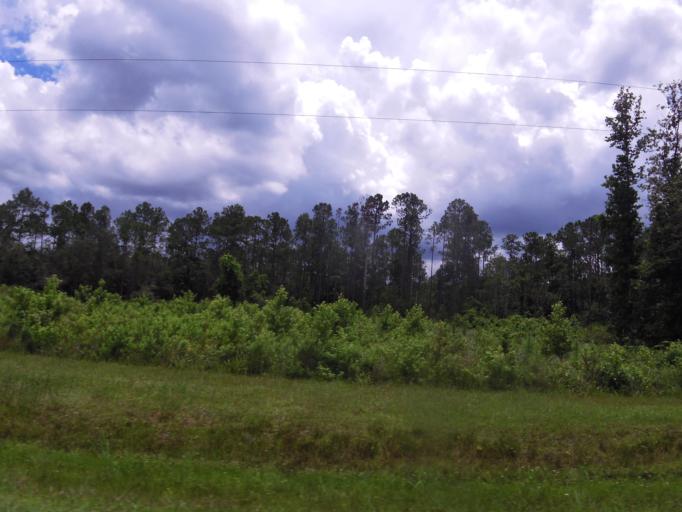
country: US
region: Florida
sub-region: Flagler County
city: Palm Coast
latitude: 29.6554
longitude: -81.3356
